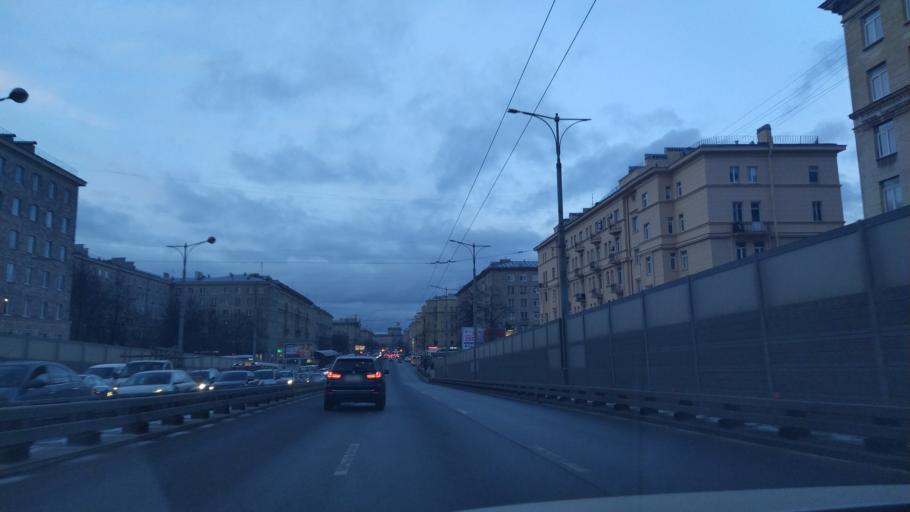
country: RU
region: St.-Petersburg
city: Avtovo
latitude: 59.8660
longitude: 30.2611
